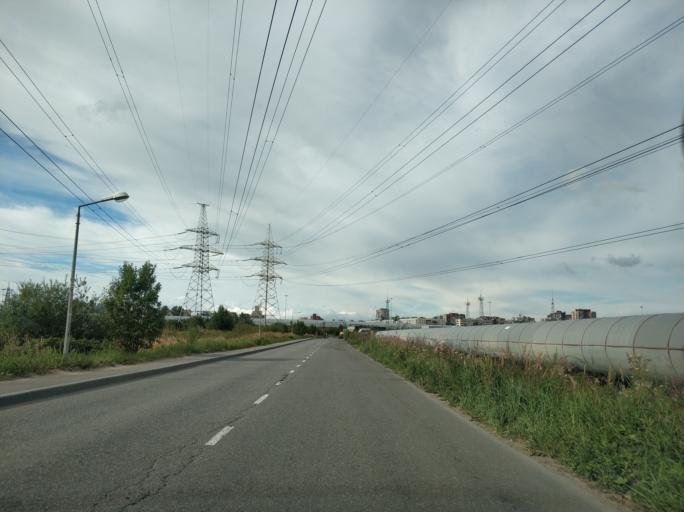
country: RU
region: Leningrad
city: Murino
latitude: 60.0471
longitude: 30.4365
